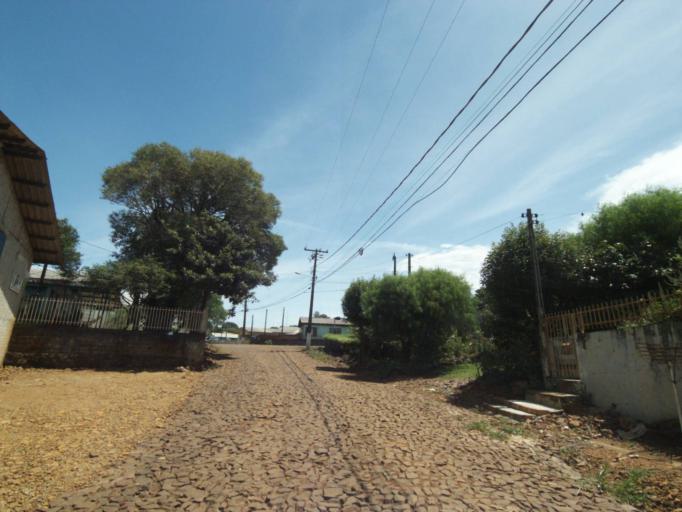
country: BR
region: Parana
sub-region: Guaraniacu
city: Guaraniacu
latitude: -25.0919
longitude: -52.8739
